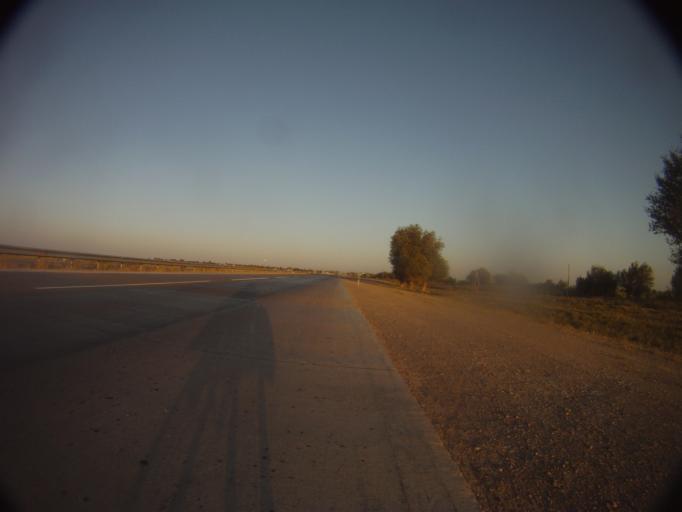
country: KZ
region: Ongtustik Qazaqstan
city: Turkestan
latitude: 43.2673
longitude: 68.3583
